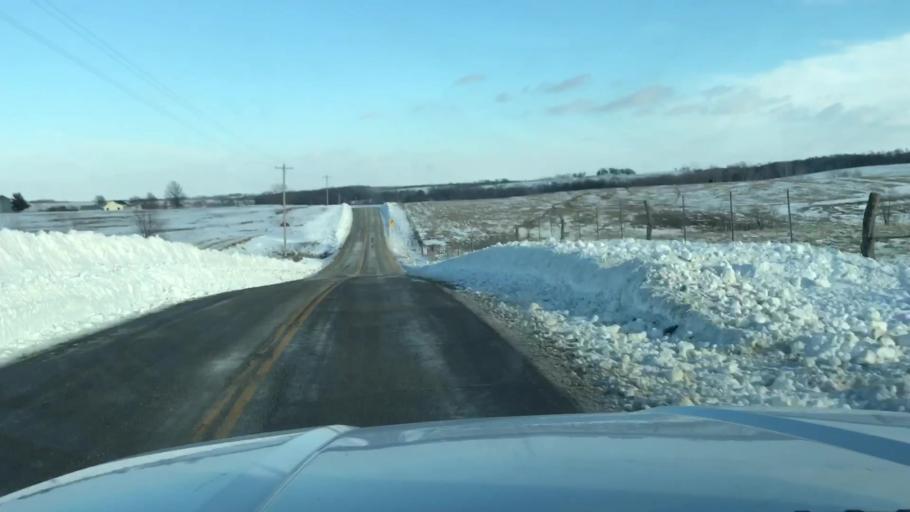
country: US
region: Missouri
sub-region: Holt County
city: Oregon
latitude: 40.1006
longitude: -94.9823
